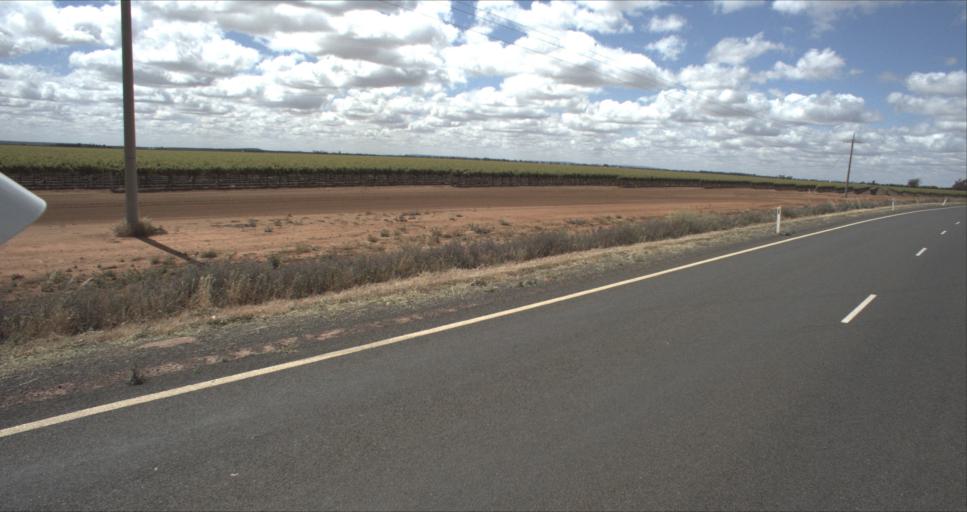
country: AU
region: New South Wales
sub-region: Murrumbidgee Shire
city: Darlington Point
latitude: -34.4747
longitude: 146.1474
